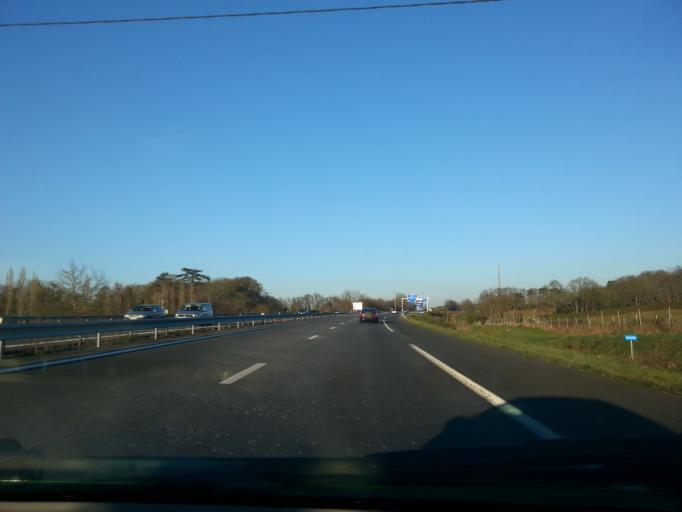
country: FR
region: Pays de la Loire
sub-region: Departement de la Sarthe
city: La Chapelle-Saint-Aubin
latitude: 48.0302
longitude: 0.1350
